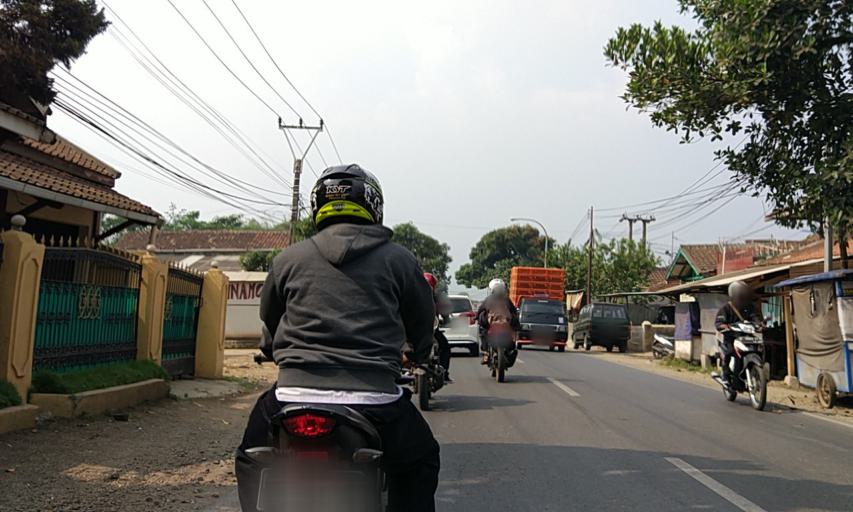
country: ID
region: West Java
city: Banjaran
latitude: -7.0512
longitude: 107.5768
